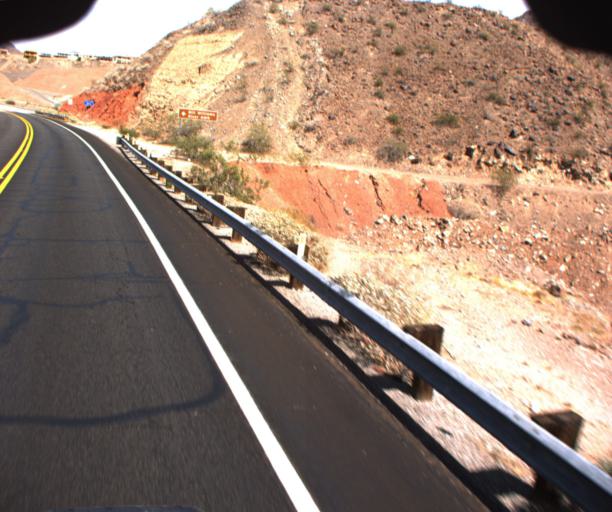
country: US
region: Arizona
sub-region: La Paz County
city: Cienega Springs
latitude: 34.2889
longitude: -114.1068
